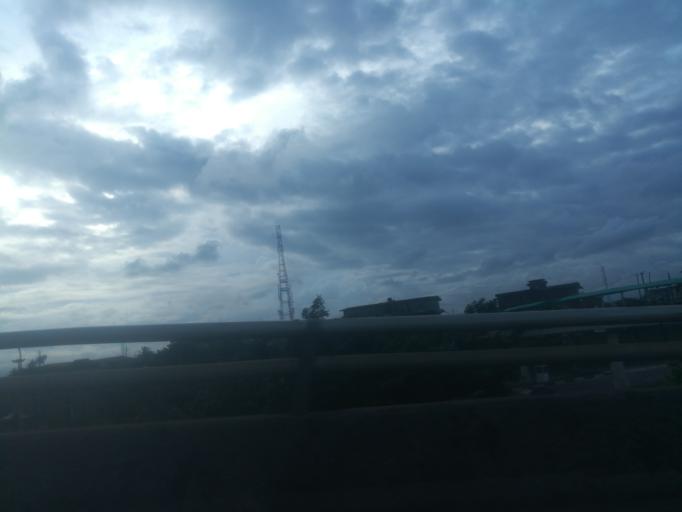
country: NG
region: Lagos
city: Somolu
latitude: 6.5513
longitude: 3.3972
